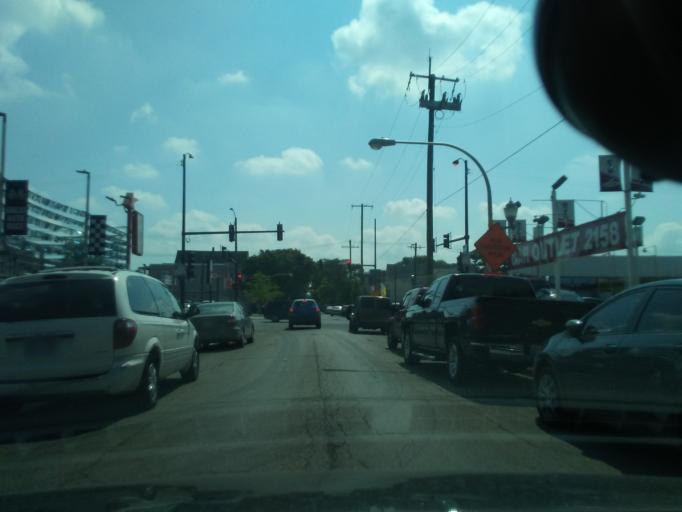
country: US
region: Illinois
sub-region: Cook County
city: Oak Park
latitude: 41.9206
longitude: -87.7468
